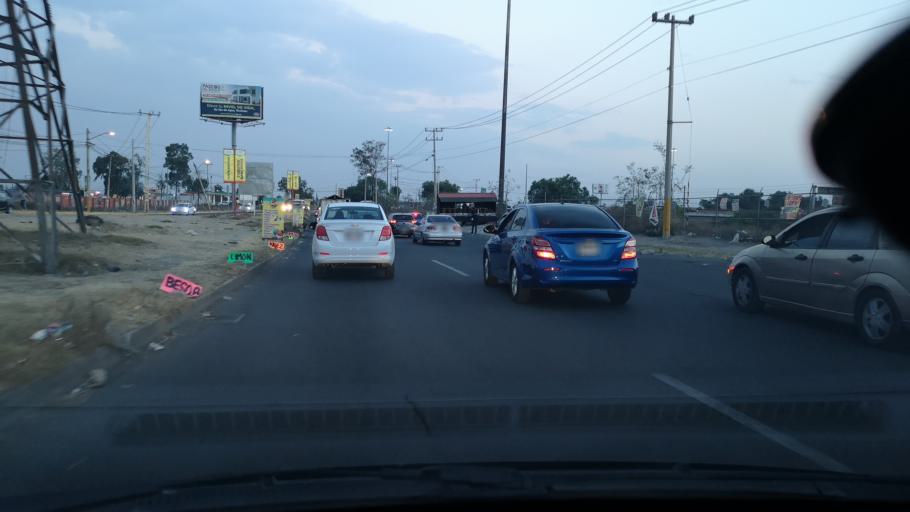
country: MX
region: Mexico
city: Ecatepec
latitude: 19.6158
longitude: -99.0405
